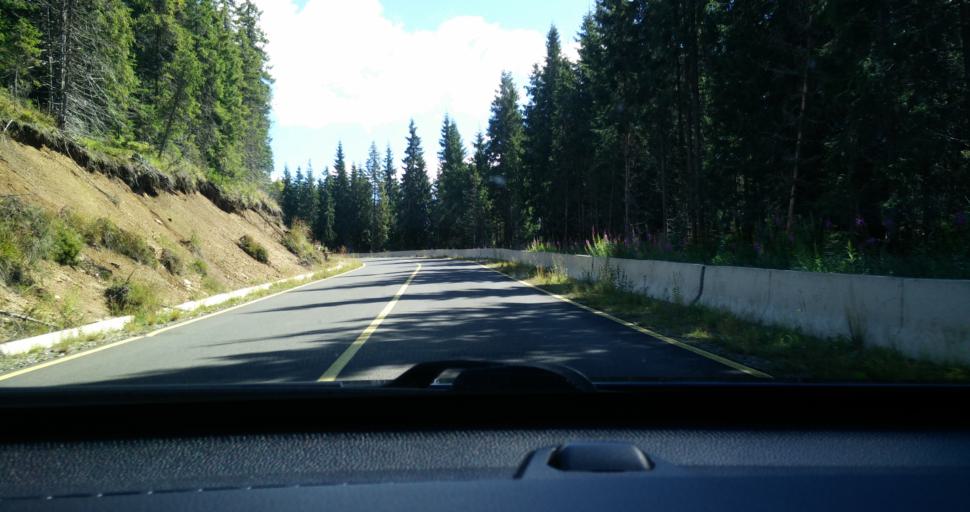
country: RO
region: Hunedoara
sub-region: Oras Petrila
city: Petrila
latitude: 45.4632
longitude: 23.6170
